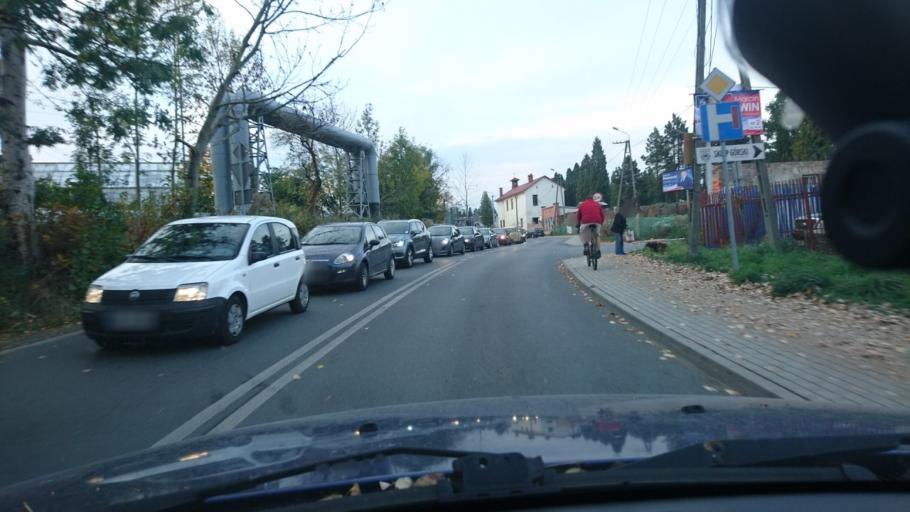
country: PL
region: Silesian Voivodeship
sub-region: Bielsko-Biala
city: Bielsko-Biala
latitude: 49.8188
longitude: 19.0596
